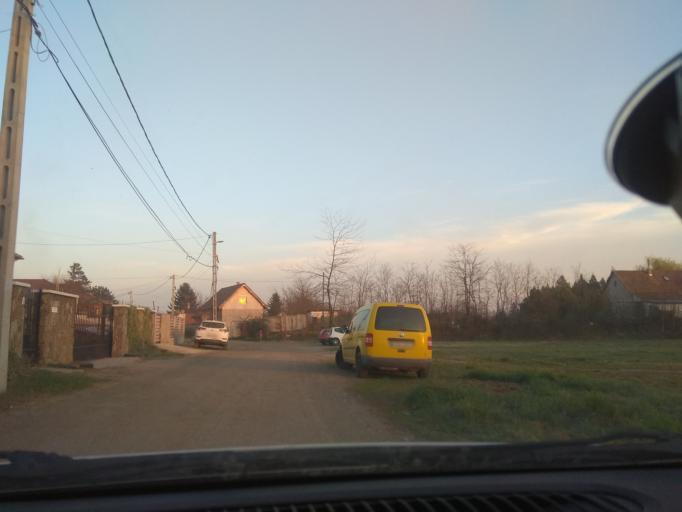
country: HU
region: Pest
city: Szigetszentmiklos
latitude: 47.3248
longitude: 19.0306
